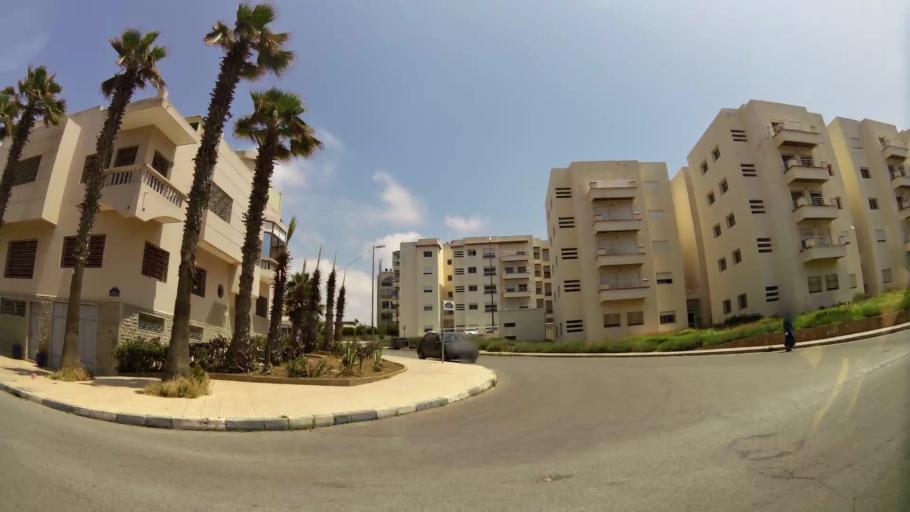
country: MA
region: Rabat-Sale-Zemmour-Zaer
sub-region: Skhirate-Temara
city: Temara
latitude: 33.9760
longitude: -6.8963
